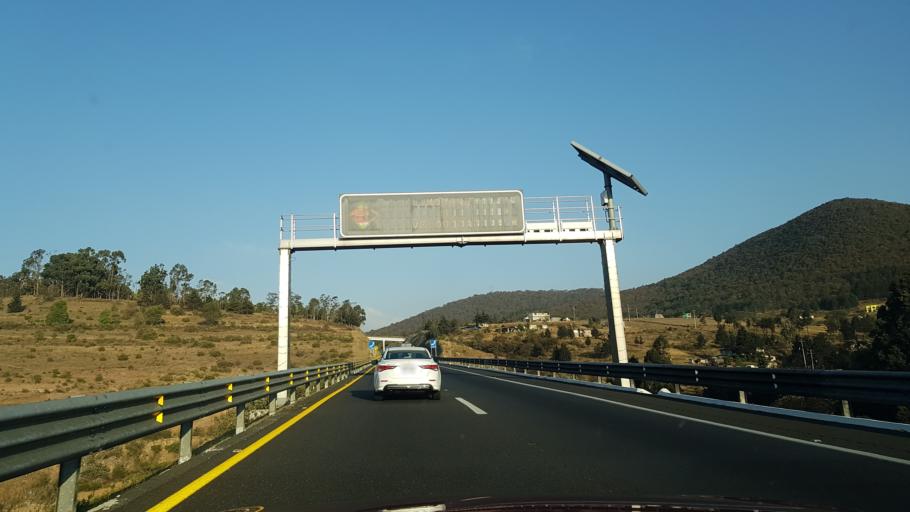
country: MX
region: Mexico
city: Temascalcingo de Jose Maria Velazco
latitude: 19.8546
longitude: -100.0315
